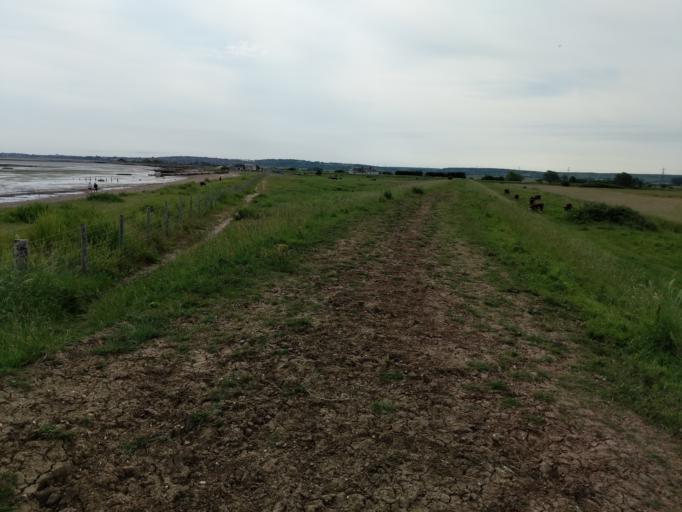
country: GB
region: England
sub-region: Kent
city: Dunkirk
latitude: 51.3453
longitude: 0.9526
